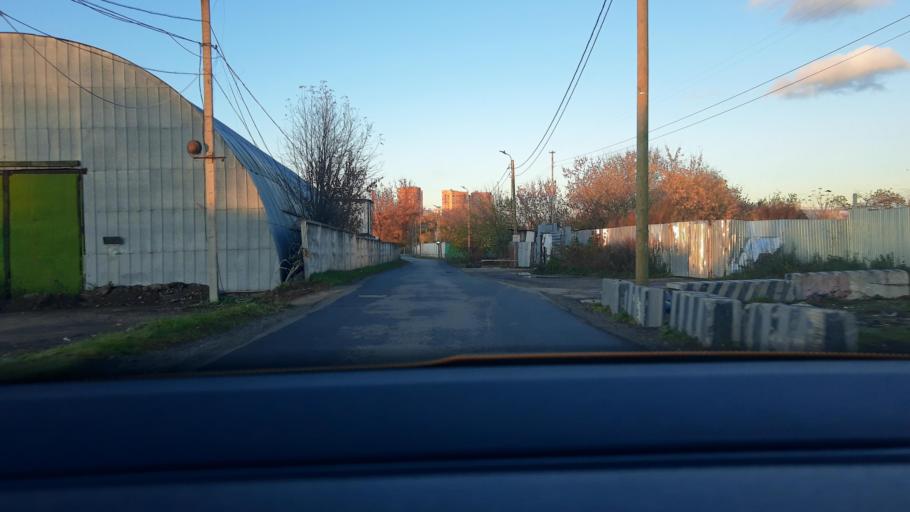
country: RU
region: Moscow
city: Strogino
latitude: 55.7865
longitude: 37.3972
